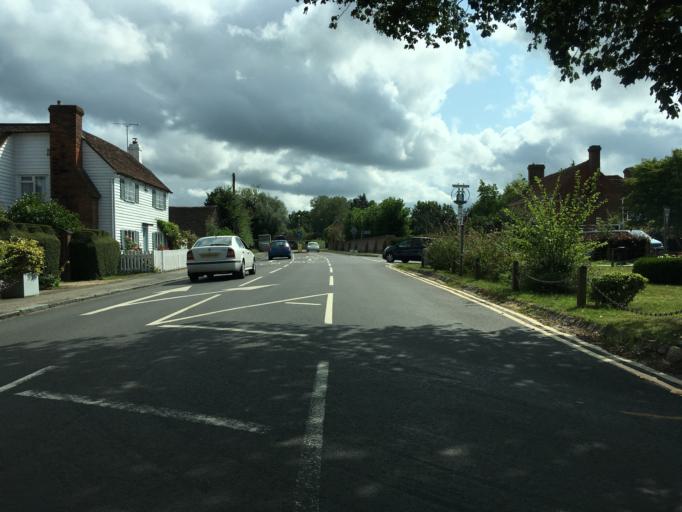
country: GB
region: England
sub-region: Kent
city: Headcorn
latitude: 51.1149
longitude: 0.6436
